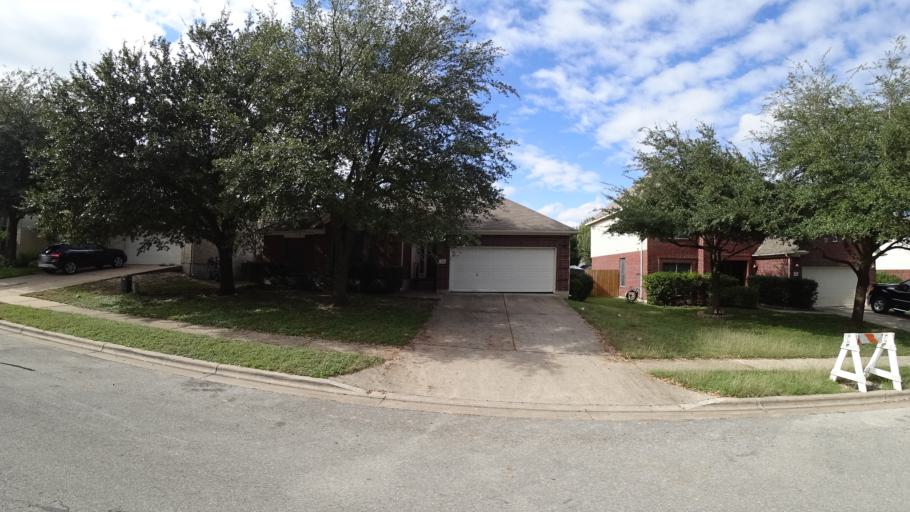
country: US
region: Texas
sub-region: Travis County
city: Pflugerville
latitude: 30.4391
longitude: -97.6377
